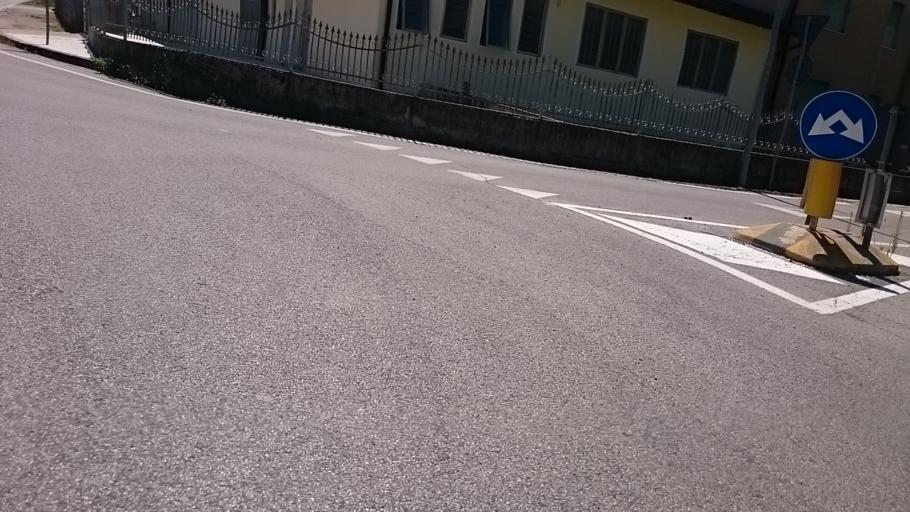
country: IT
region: Veneto
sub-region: Provincia di Venezia
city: Pianiga
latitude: 45.4672
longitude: 11.9878
